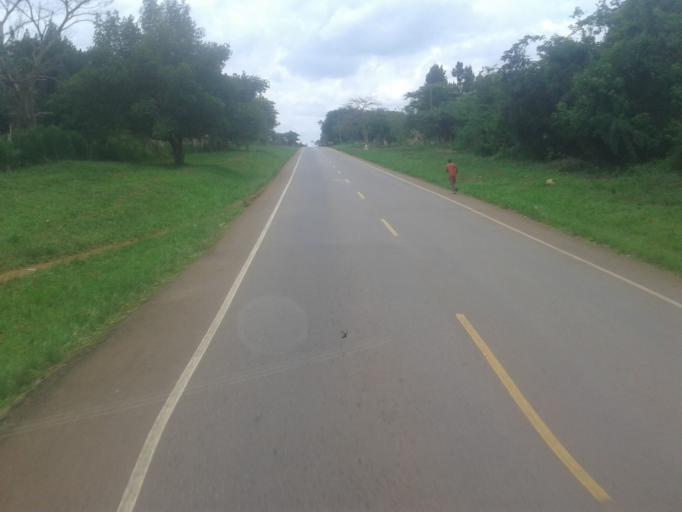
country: UG
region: Central Region
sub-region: Luwero District
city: Luwero
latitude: 1.0372
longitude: 32.4679
